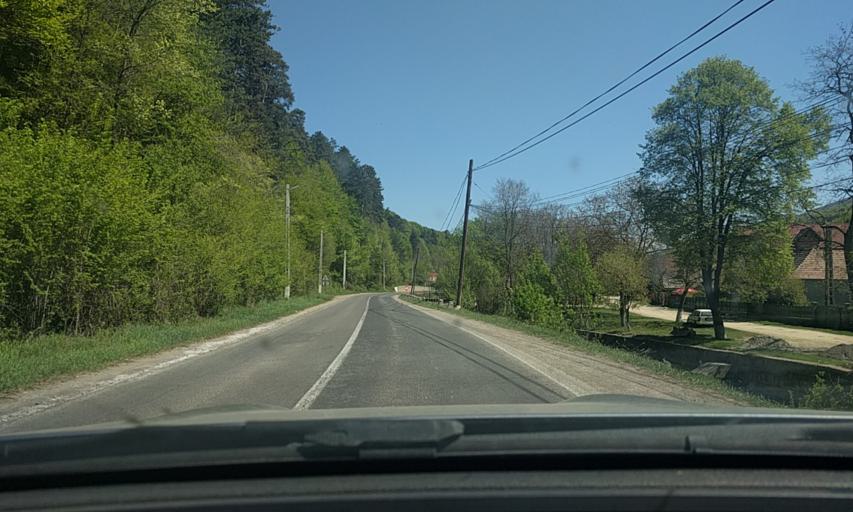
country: RO
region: Brasov
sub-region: Comuna Teliu
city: Teliu
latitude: 45.6949
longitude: 25.8687
